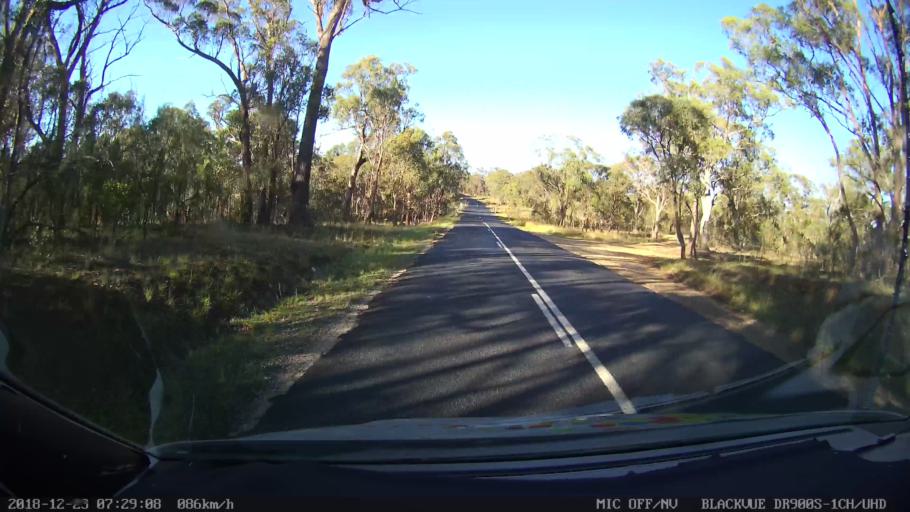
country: AU
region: New South Wales
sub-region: Armidale Dumaresq
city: Enmore
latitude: -30.4925
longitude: 152.1592
